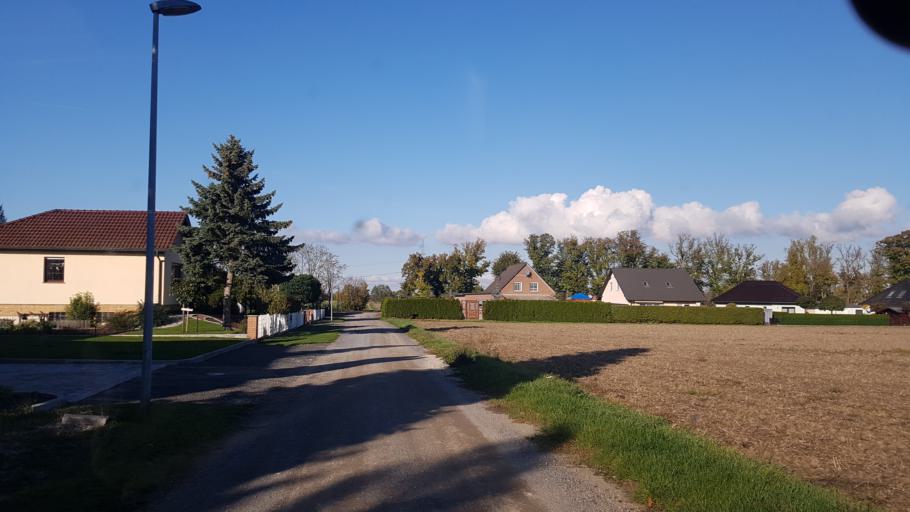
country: DE
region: Brandenburg
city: Doberlug-Kirchhain
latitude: 51.6364
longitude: 13.5477
